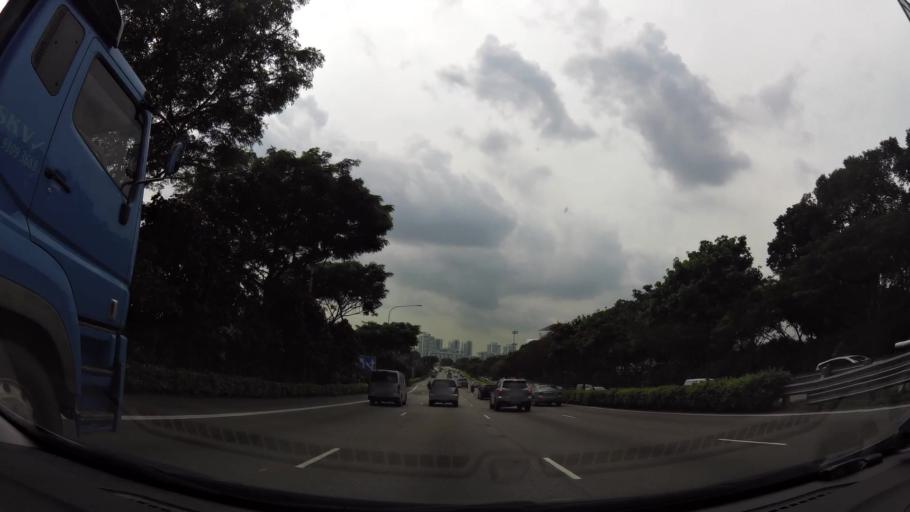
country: MY
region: Johor
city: Kampung Pasir Gudang Baru
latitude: 1.3822
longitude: 103.8584
